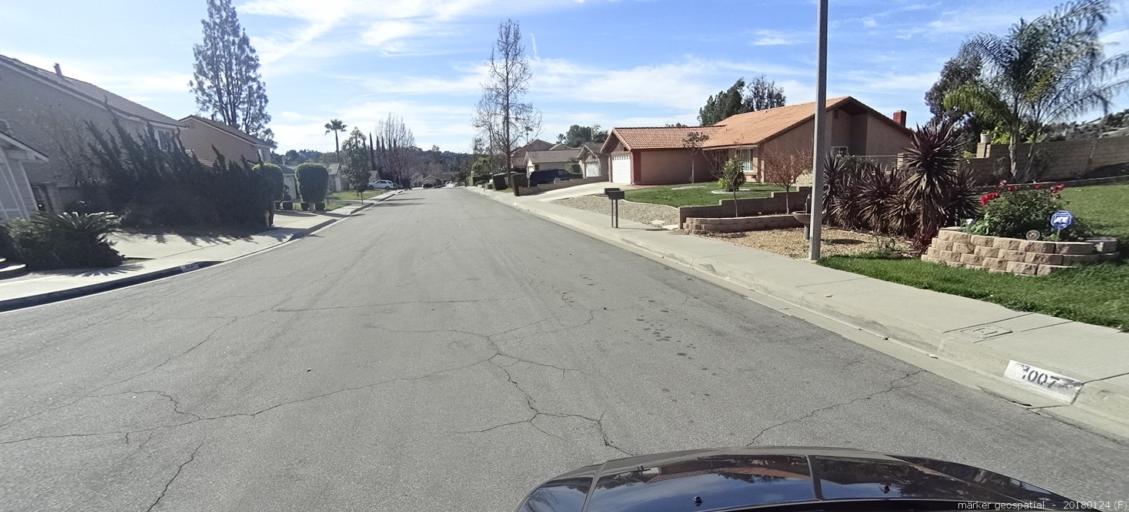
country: US
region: California
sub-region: Los Angeles County
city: Diamond Bar
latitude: 34.0056
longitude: -117.8075
